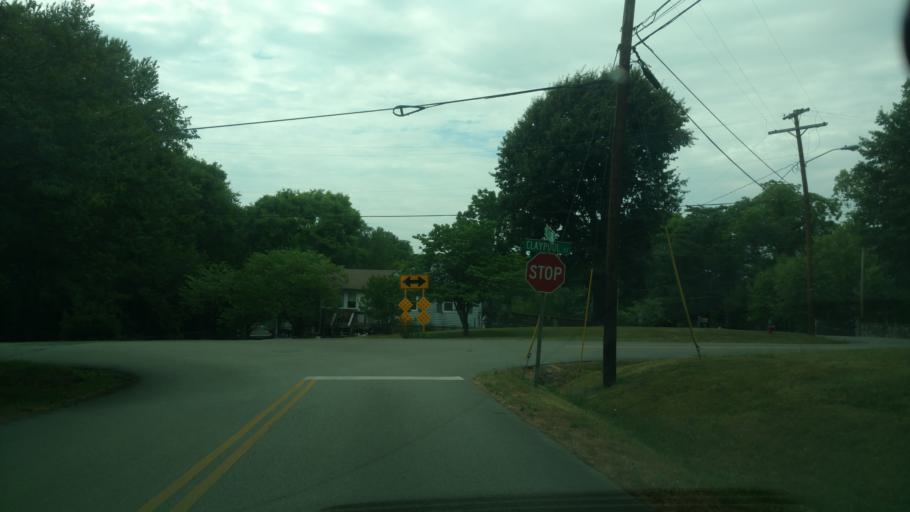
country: US
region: Tennessee
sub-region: Davidson County
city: Lakewood
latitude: 36.2151
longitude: -86.7076
